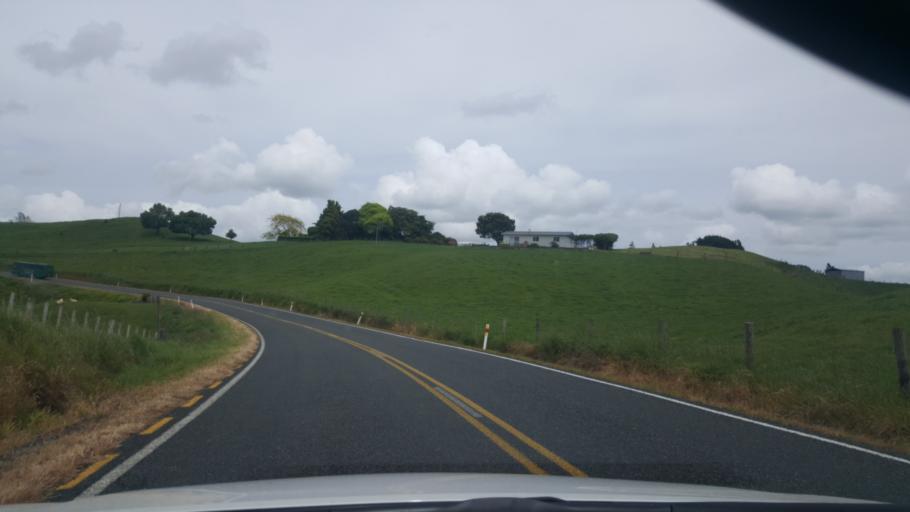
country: NZ
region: Waikato
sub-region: Matamata-Piako District
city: Matamata
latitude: -37.8757
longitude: 175.6853
